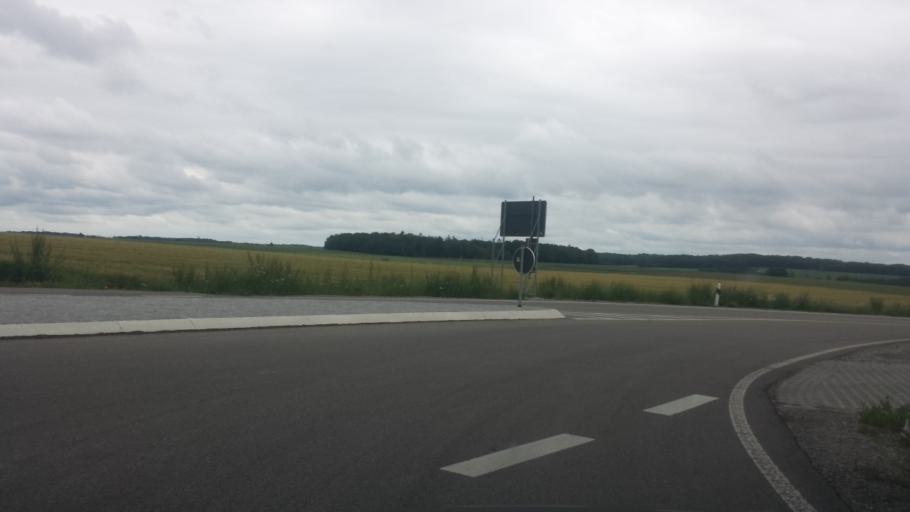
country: DE
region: Baden-Wuerttemberg
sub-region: Regierungsbezirk Stuttgart
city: Rot am See
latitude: 49.2783
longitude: 10.0080
